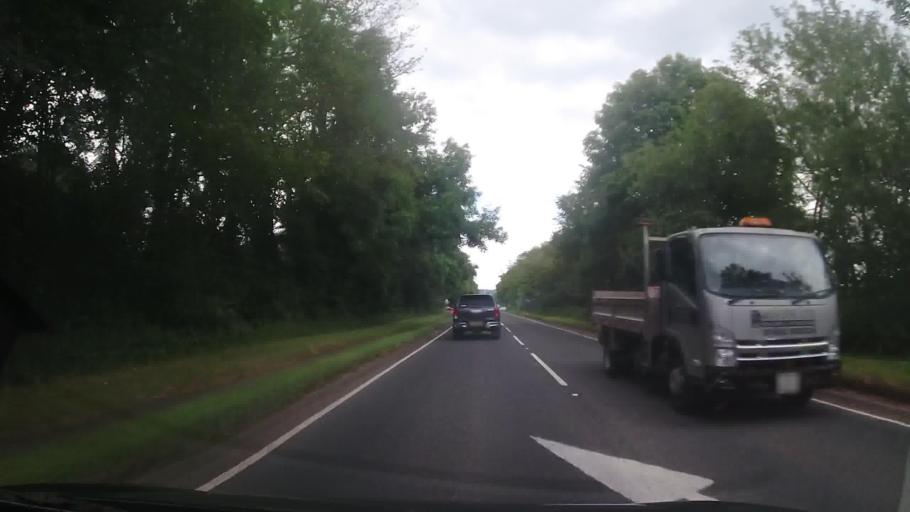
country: GB
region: England
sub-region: Herefordshire
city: Wellington
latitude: 52.1037
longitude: -2.7285
